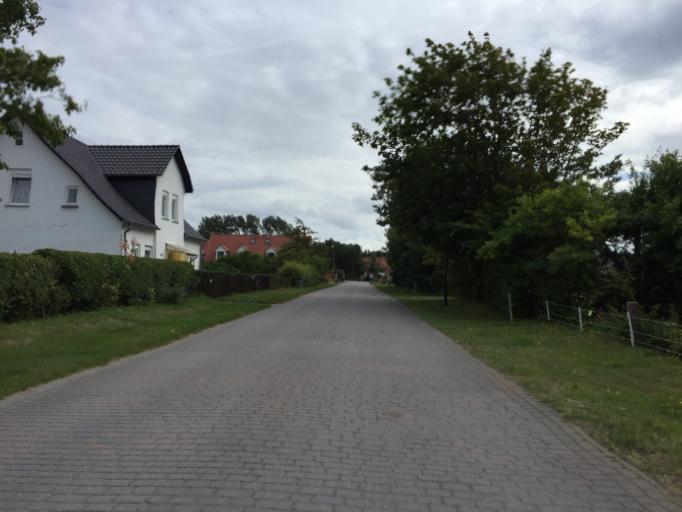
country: DE
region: Mecklenburg-Vorpommern
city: Hiddensee
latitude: 54.5634
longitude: 13.1030
